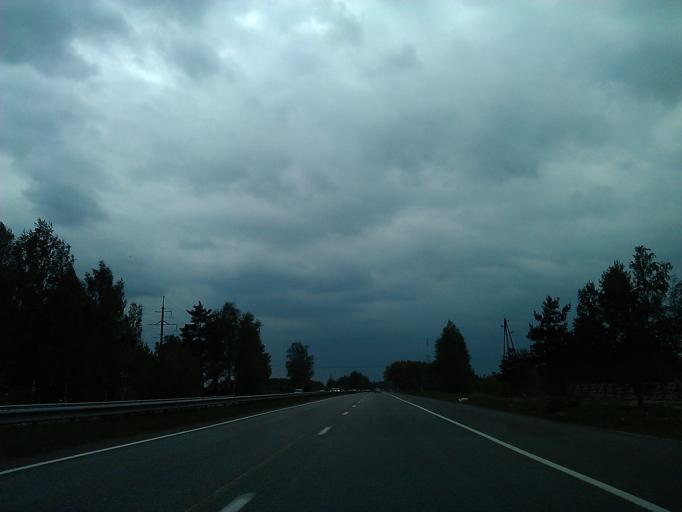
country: LV
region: Marupe
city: Marupe
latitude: 56.8232
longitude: 24.0228
